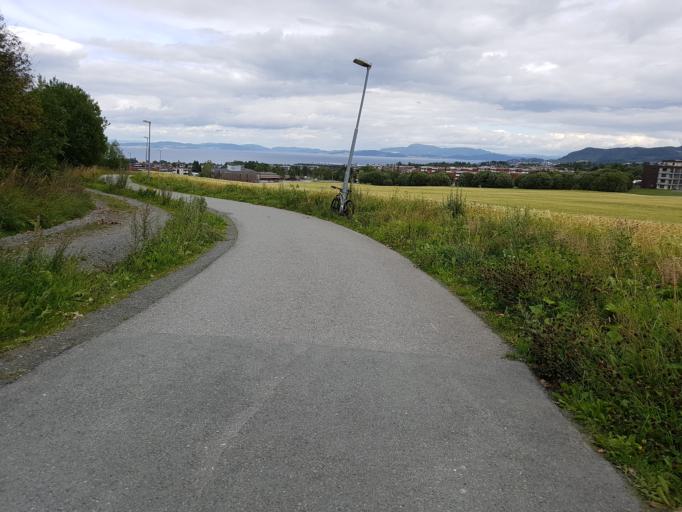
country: NO
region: Sor-Trondelag
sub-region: Trondheim
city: Trondheim
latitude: 63.4145
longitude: 10.4722
